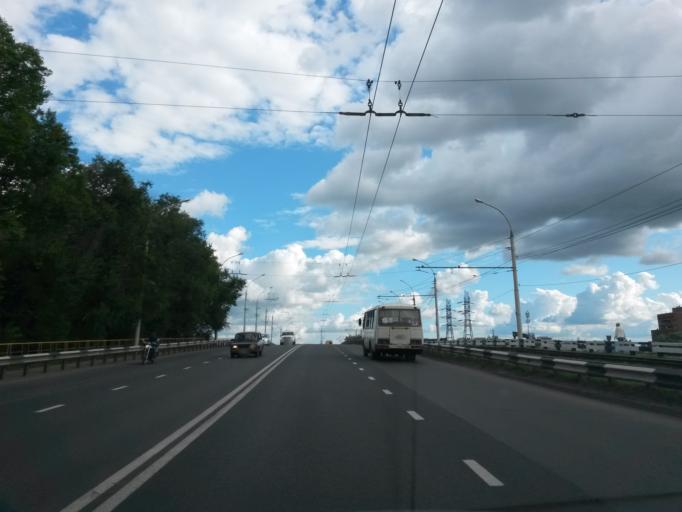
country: RU
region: Jaroslavl
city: Yaroslavl
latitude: 57.6448
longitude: 39.8526
